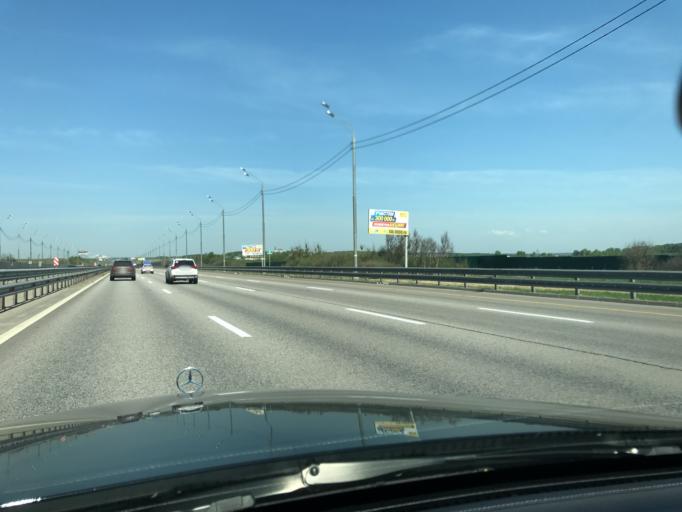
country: RU
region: Moskovskaya
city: Pavlovskaya Sloboda
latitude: 55.7920
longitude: 37.0541
